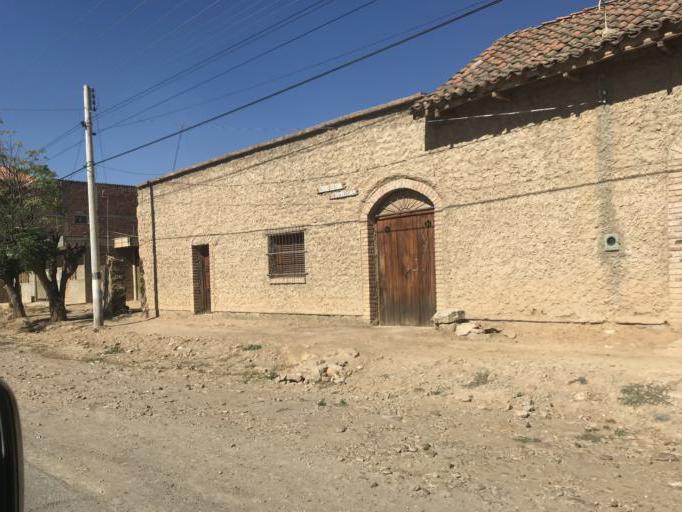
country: BO
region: Cochabamba
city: Cliza
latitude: -17.5783
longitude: -65.9083
